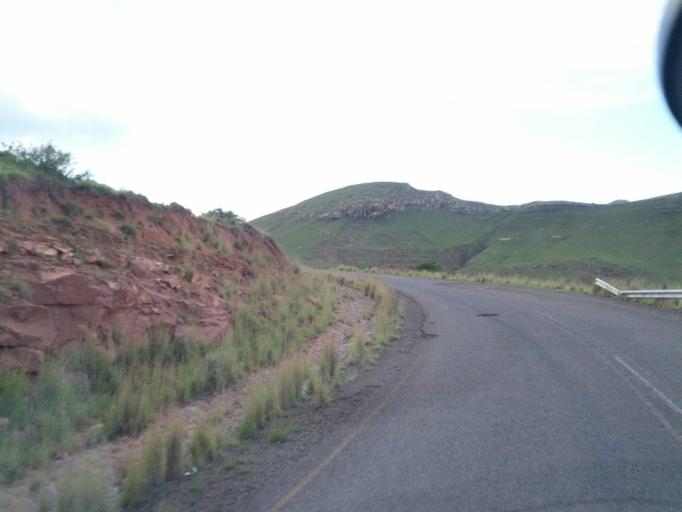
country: LS
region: Qacha's Nek
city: Qacha's Nek
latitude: -30.0538
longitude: 28.5032
